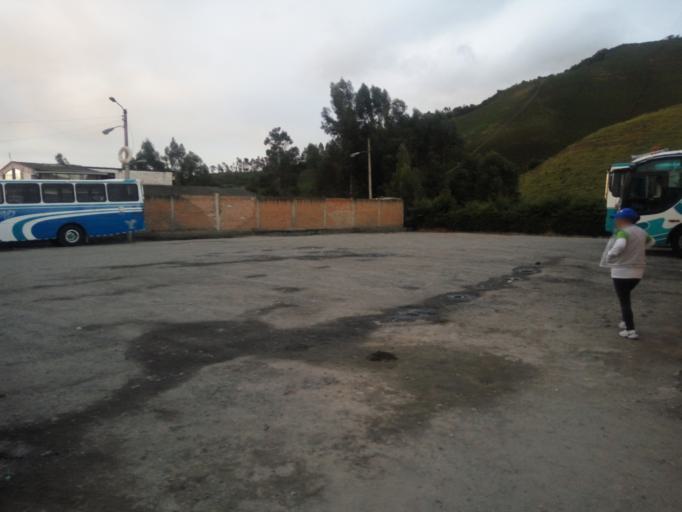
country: EC
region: Carchi
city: Tulcan
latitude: 0.7760
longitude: -77.7407
